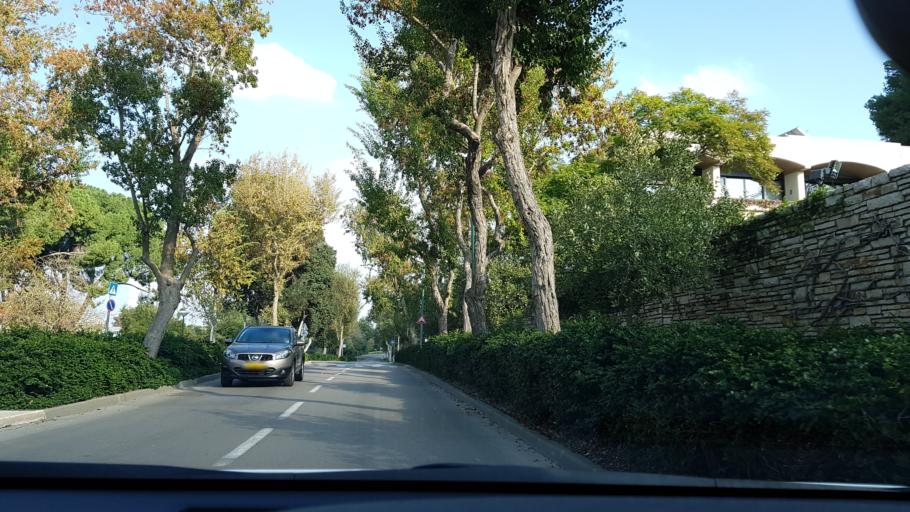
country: IL
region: Central District
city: Ness Ziona
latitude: 31.9073
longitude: 34.8127
